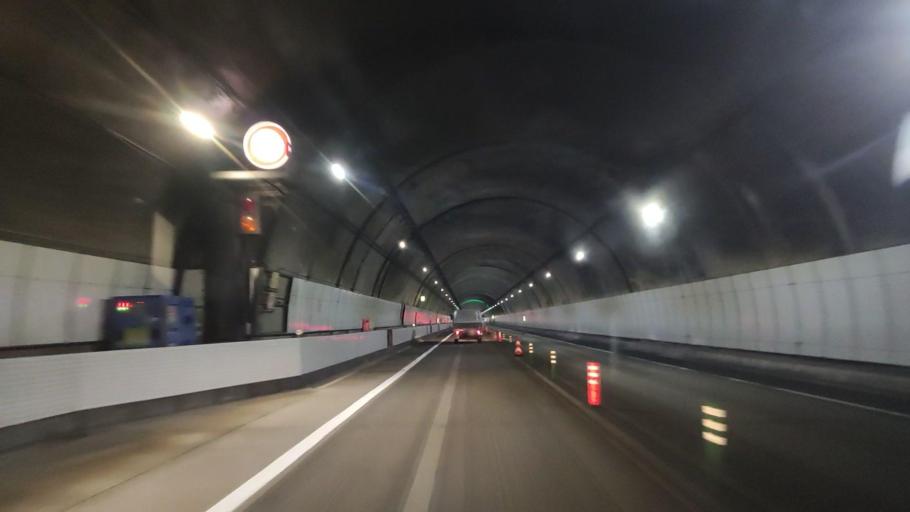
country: JP
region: Gifu
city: Takayama
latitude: 36.1933
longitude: 137.5655
